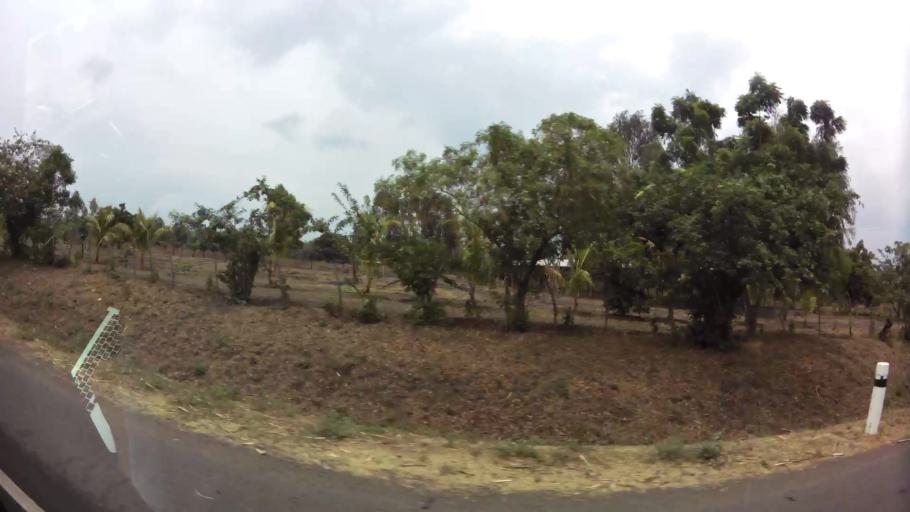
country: NI
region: Chinandega
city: Posoltega
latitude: 12.5517
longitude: -86.9368
